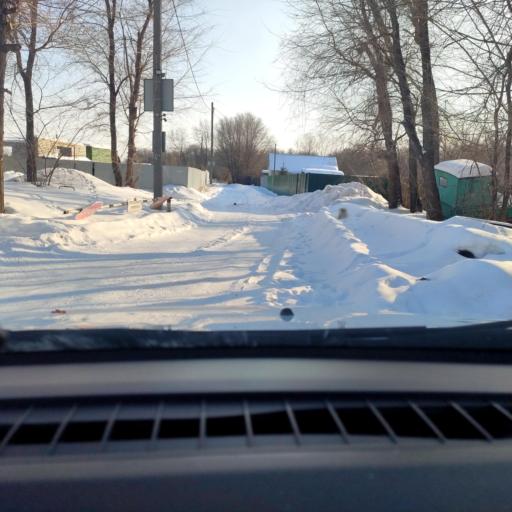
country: RU
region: Samara
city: Samara
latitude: 53.1289
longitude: 50.2599
